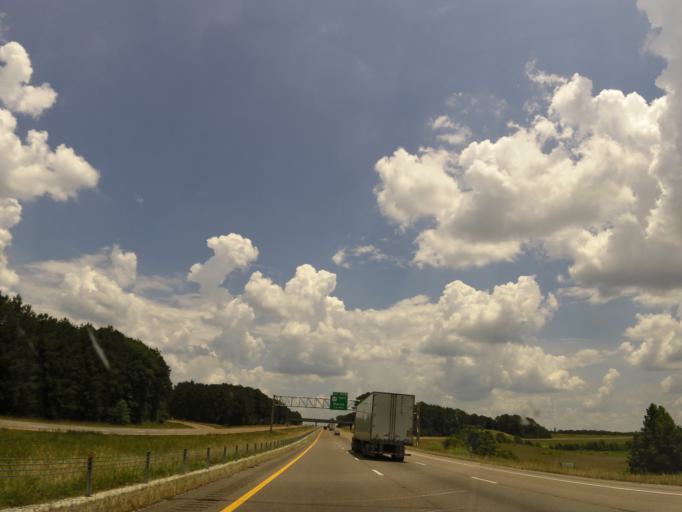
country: US
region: Mississippi
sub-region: Lauderdale County
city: Marion
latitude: 32.3820
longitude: -88.6431
